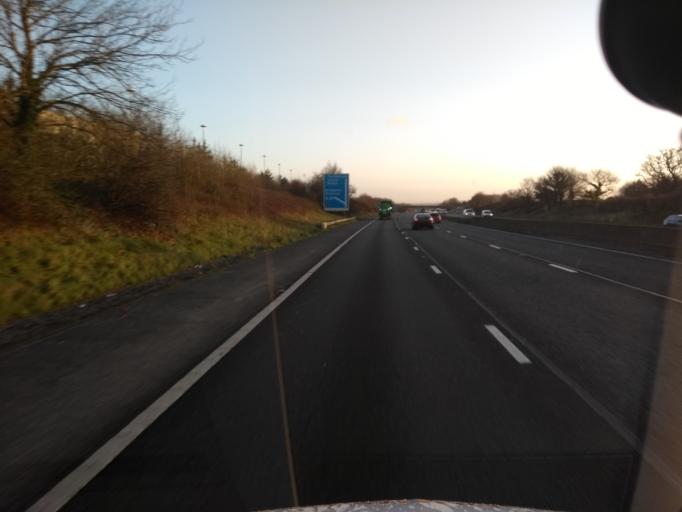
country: GB
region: England
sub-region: Somerset
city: North Petherton
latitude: 51.0974
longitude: -2.9991
